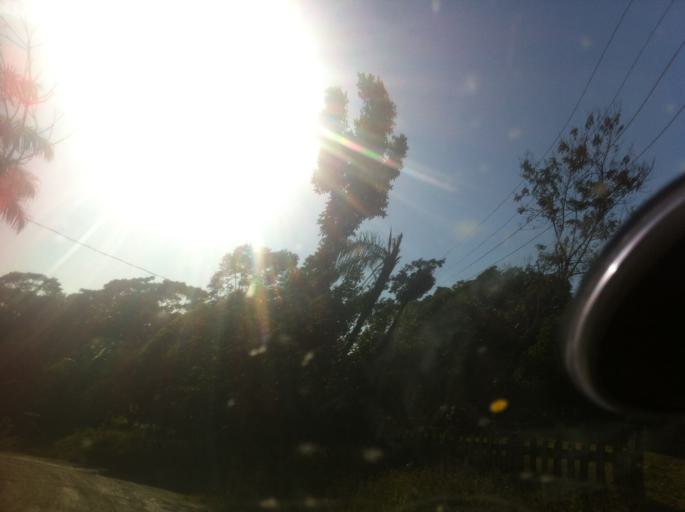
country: CR
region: Alajuela
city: Los Chiles
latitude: 11.0453
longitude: -84.4658
